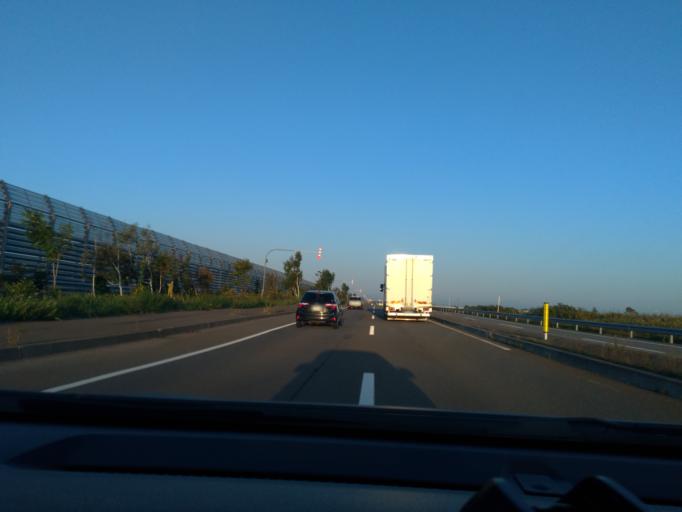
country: JP
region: Hokkaido
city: Tobetsu
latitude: 43.1826
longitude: 141.5062
